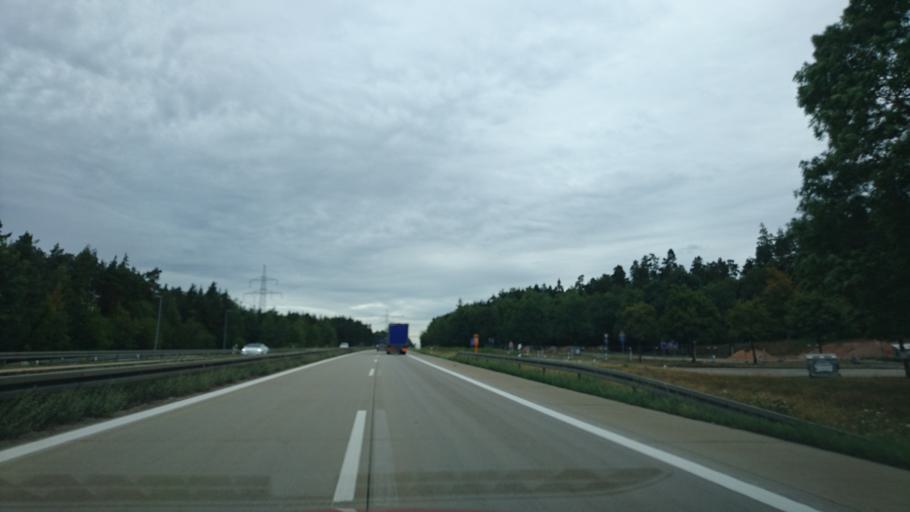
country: DE
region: Bavaria
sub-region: Upper Palatinate
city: Luhe-Wildenau
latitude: 49.5710
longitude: 12.1228
